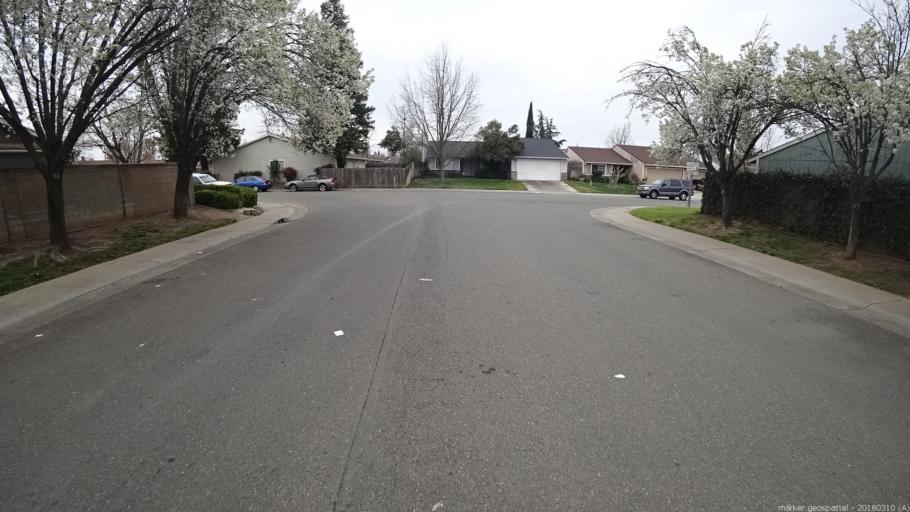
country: US
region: California
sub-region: Sacramento County
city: Florin
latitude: 38.4814
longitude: -121.3824
